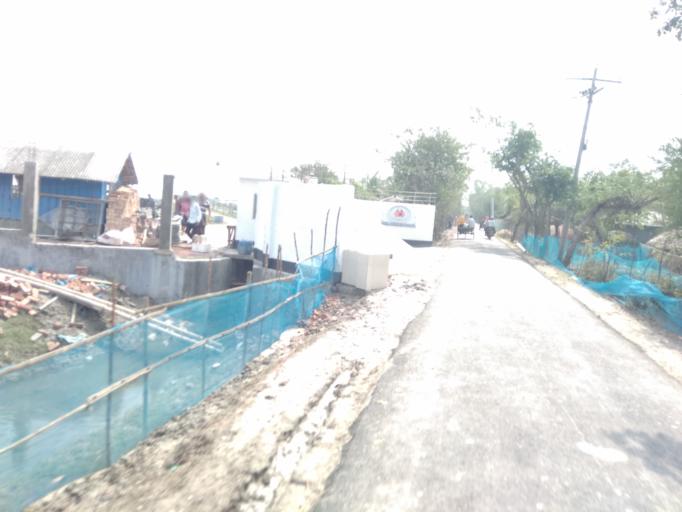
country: IN
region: West Bengal
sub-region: North 24 Parganas
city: Gosaba
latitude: 22.2614
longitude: 89.2243
